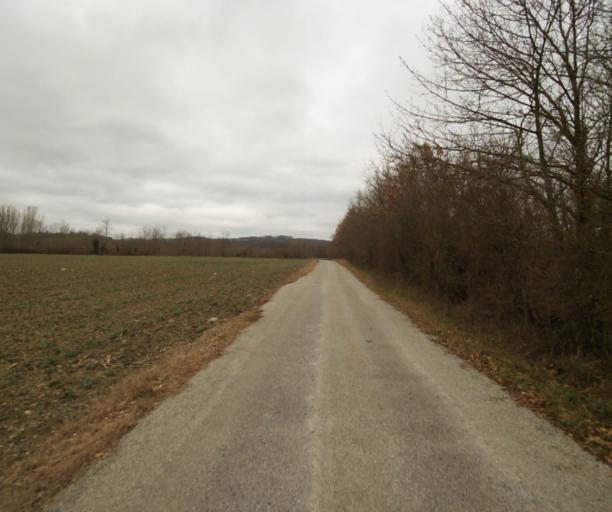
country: FR
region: Midi-Pyrenees
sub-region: Departement de l'Ariege
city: Pamiers
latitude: 43.1476
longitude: 1.5968
